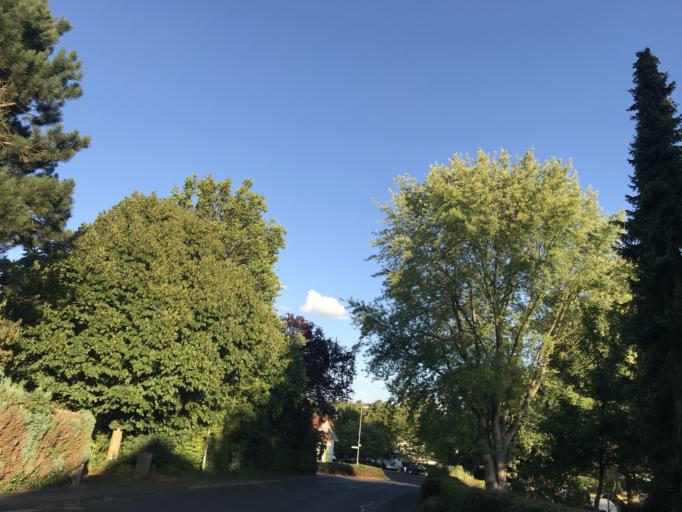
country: DE
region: Hesse
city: Lollar
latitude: 50.6641
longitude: 8.7084
